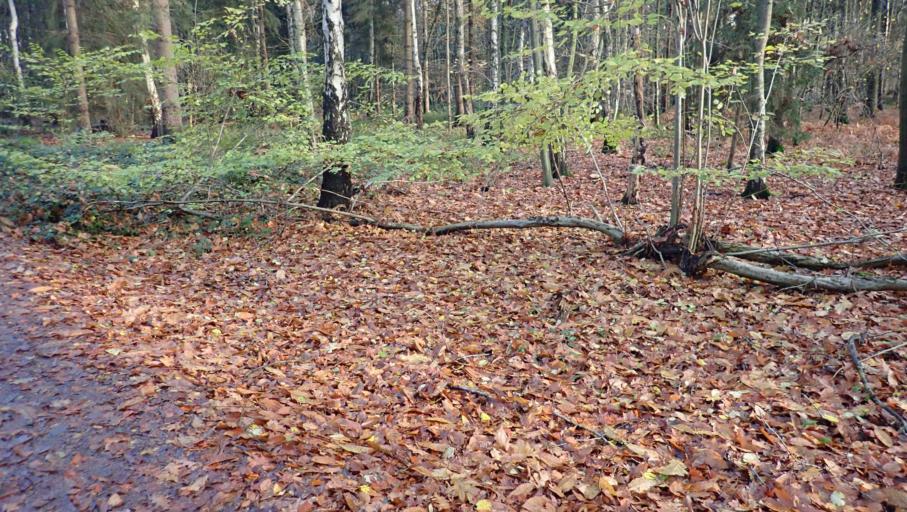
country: BE
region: Flanders
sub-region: Provincie Vlaams-Brabant
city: Opwijk
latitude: 50.9380
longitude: 4.1599
